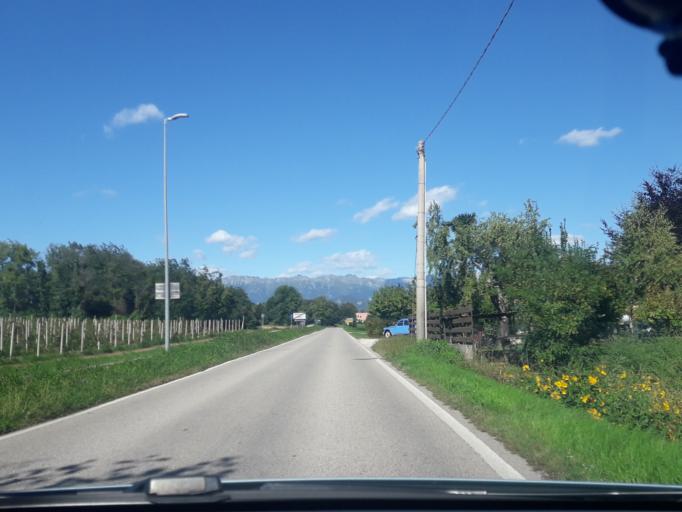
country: IT
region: Friuli Venezia Giulia
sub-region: Provincia di Udine
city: Reana del Roiale
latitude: 46.1342
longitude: 13.2163
